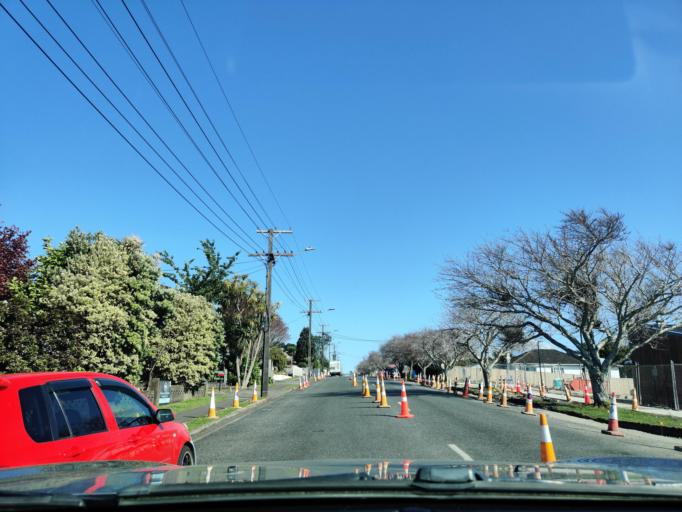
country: NZ
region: Taranaki
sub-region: New Plymouth District
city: New Plymouth
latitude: -39.0707
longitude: 174.0571
